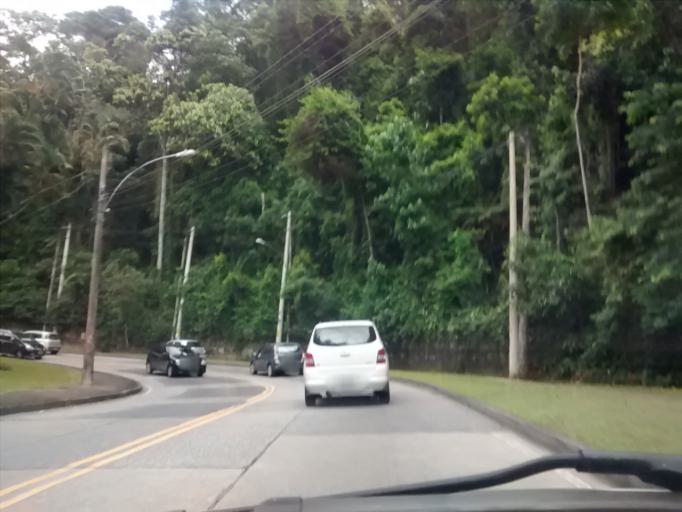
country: BR
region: Rio de Janeiro
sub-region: Rio De Janeiro
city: Rio de Janeiro
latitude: -22.9570
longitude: -43.2684
